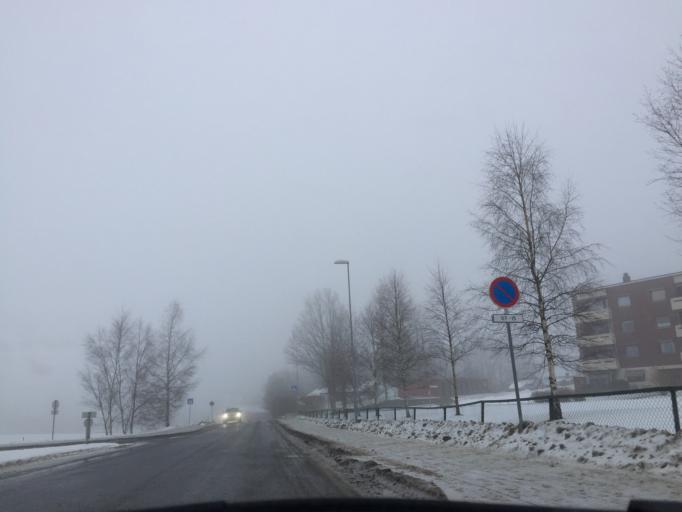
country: NO
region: Akershus
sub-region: Frogn
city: Drobak
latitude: 59.6851
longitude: 10.6613
